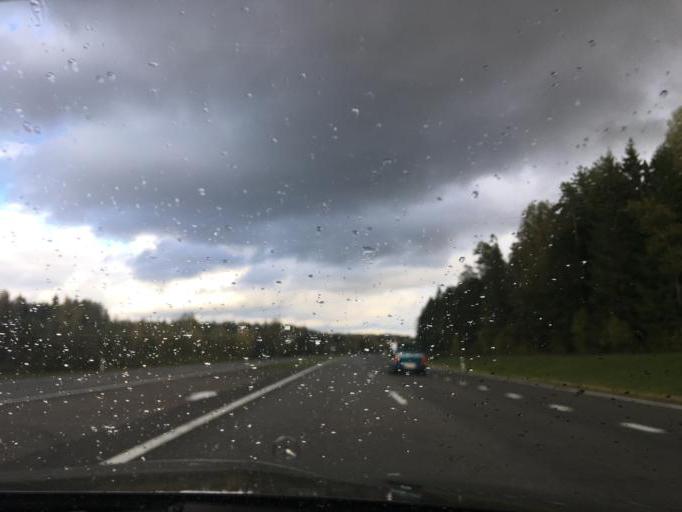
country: BY
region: Vitebsk
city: Talachyn
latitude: 54.4188
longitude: 29.5202
